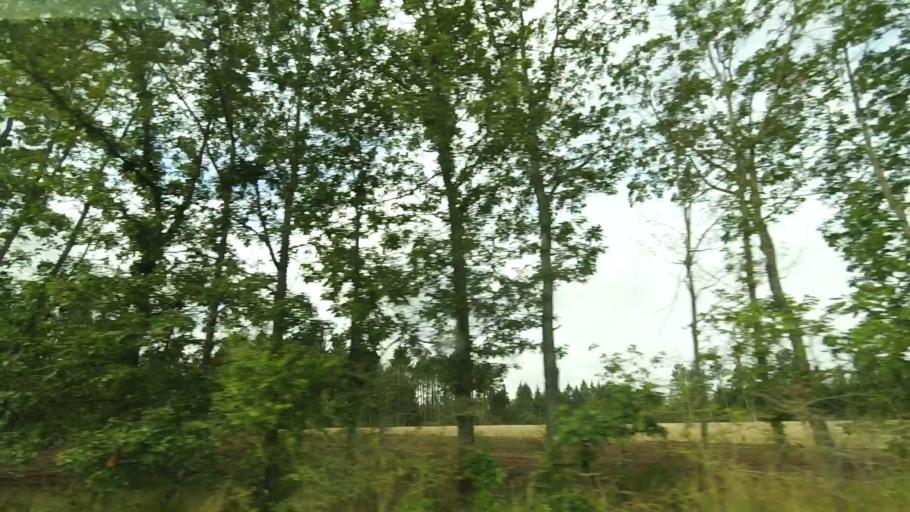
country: DK
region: Central Jutland
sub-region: Syddjurs Kommune
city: Ryomgard
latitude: 56.3616
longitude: 10.5119
